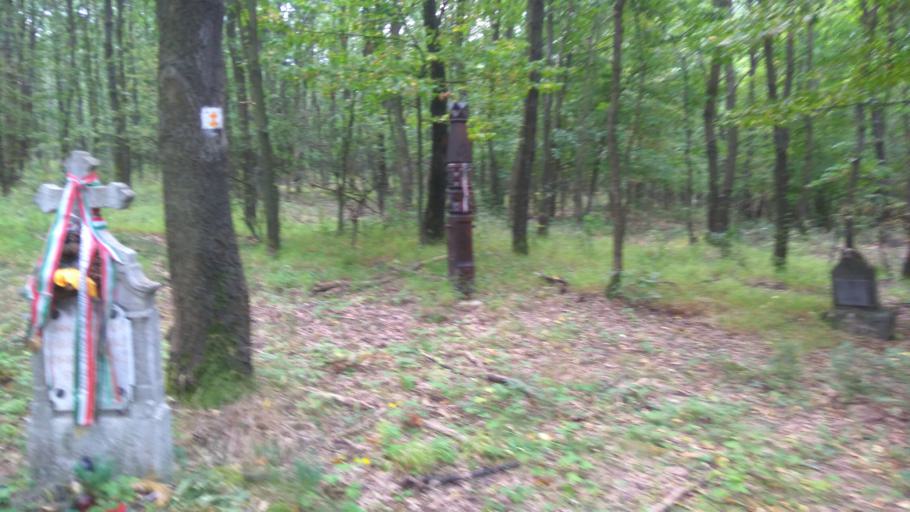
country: SK
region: Nitriansky
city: Sahy
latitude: 48.0114
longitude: 18.9438
